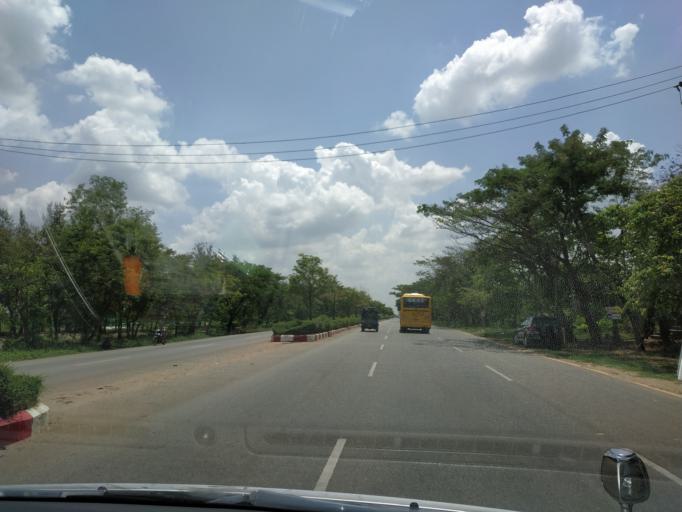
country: MM
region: Bago
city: Thanatpin
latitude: 17.0623
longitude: 96.1614
